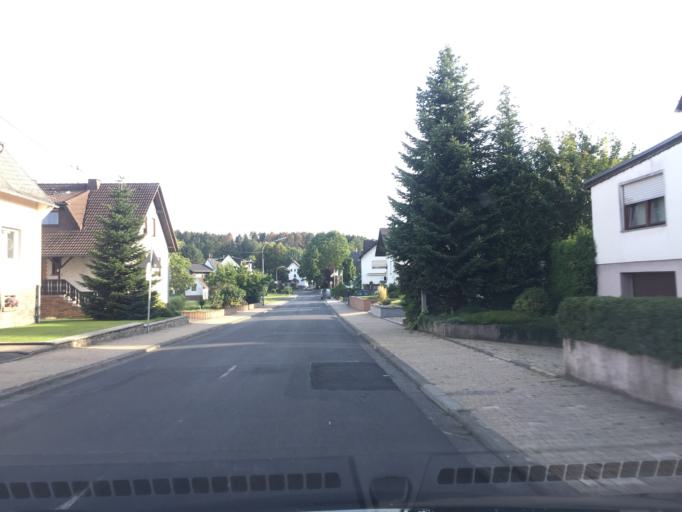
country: DE
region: Rheinland-Pfalz
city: Grossholbach
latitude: 50.4470
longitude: 7.8930
